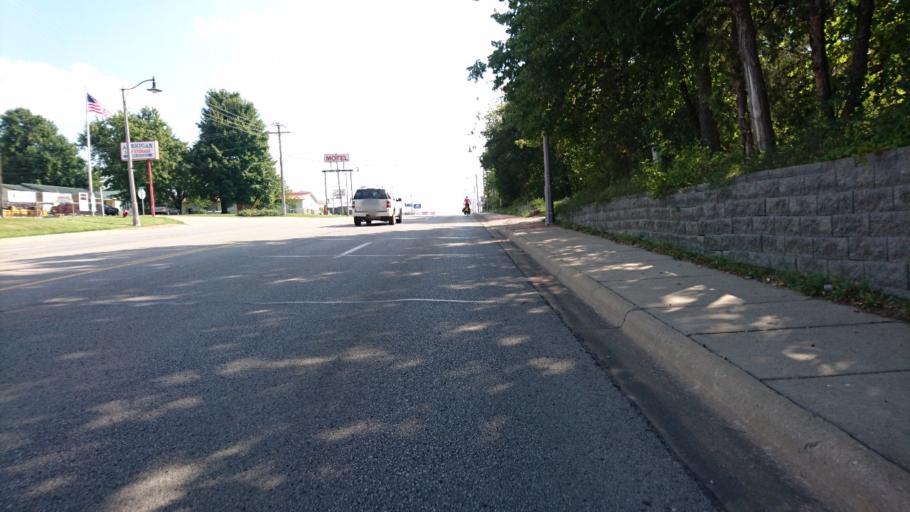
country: US
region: Missouri
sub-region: Laclede County
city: Lebanon
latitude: 37.6551
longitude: -92.6677
